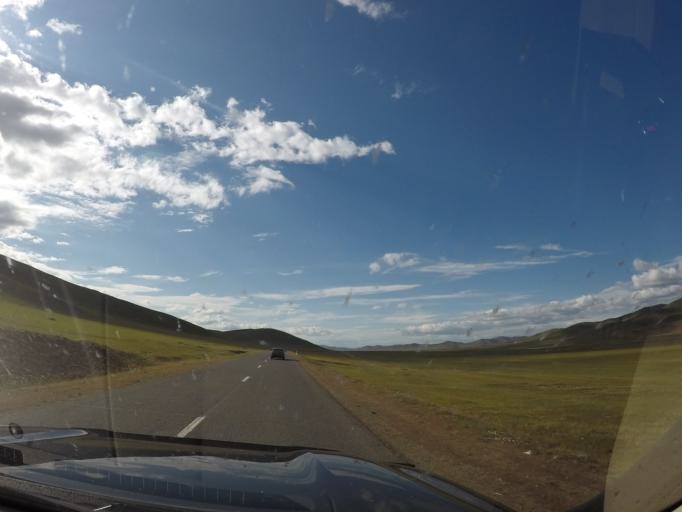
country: MN
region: Hentiy
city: Modot
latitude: 47.6929
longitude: 109.0883
